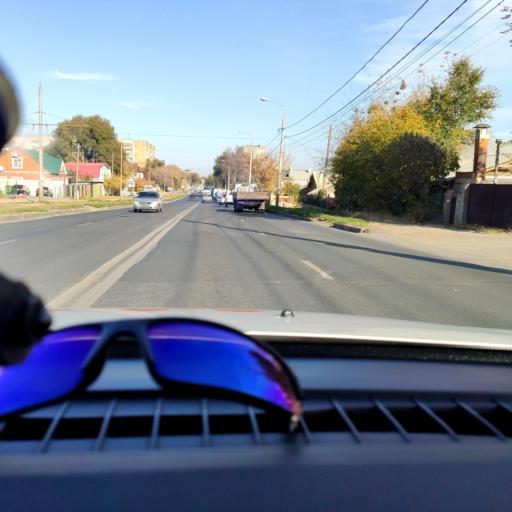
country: RU
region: Samara
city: Samara
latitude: 53.1929
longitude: 50.2147
